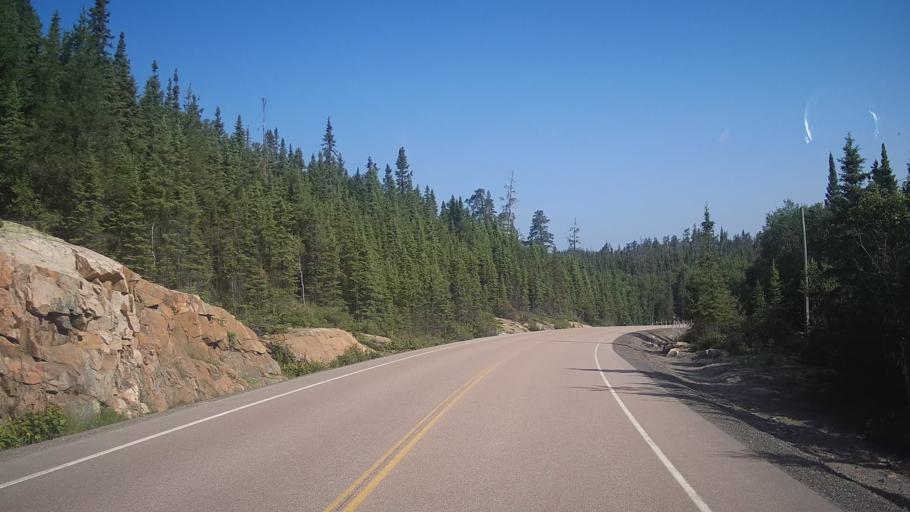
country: CA
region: Ontario
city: Rayside-Balfour
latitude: 47.0222
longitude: -81.6395
